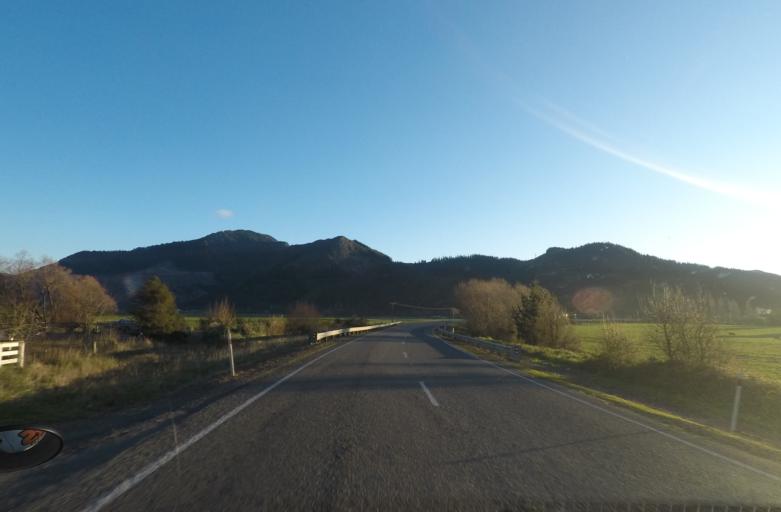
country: NZ
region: Marlborough
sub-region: Marlborough District
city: Picton
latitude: -41.2910
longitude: 173.6755
